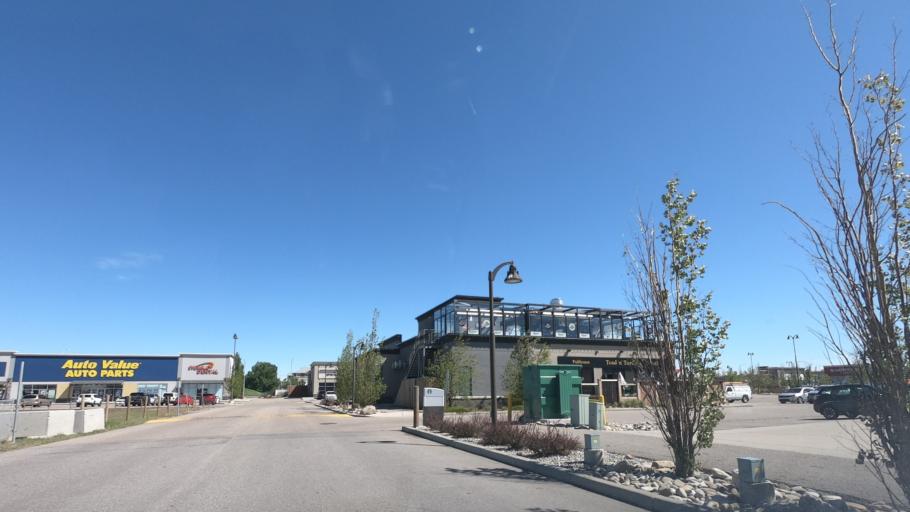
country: CA
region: Alberta
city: Airdrie
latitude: 51.2694
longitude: -113.9954
